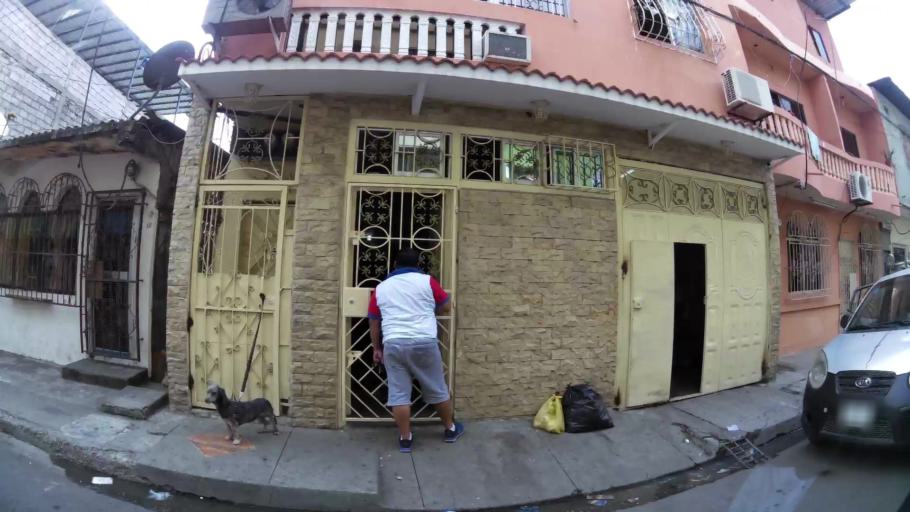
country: EC
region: Guayas
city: Guayaquil
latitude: -2.2533
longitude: -79.8965
